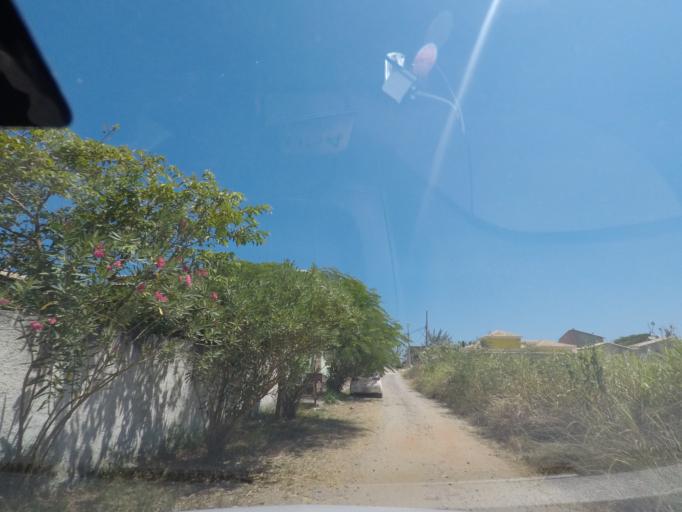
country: BR
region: Rio de Janeiro
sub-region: Marica
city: Marica
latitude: -22.9726
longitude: -42.9243
